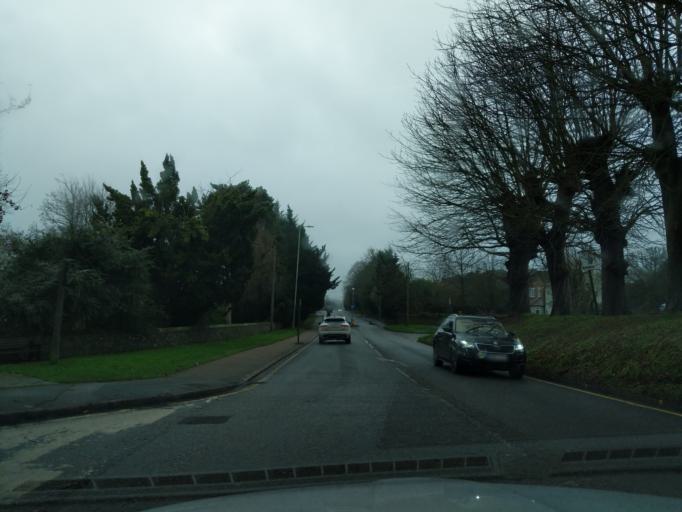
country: GB
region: England
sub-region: Hertfordshire
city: Kings Langley
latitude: 51.7110
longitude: -0.4491
